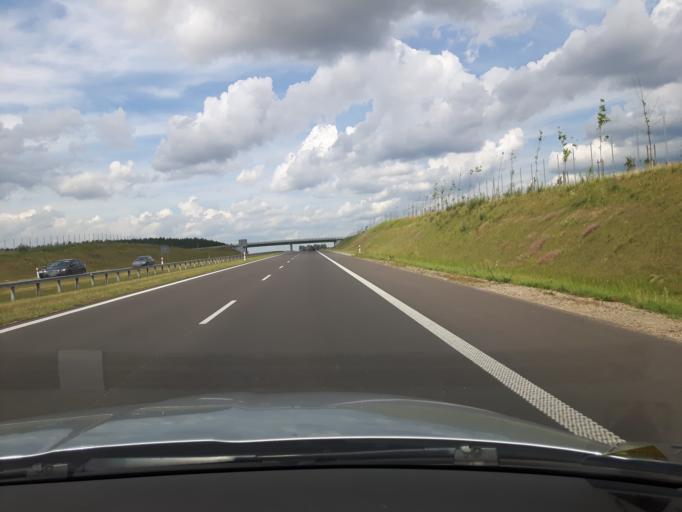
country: PL
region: Warmian-Masurian Voivodeship
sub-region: Powiat nidzicki
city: Nidzica
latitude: 53.3181
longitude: 20.4389
